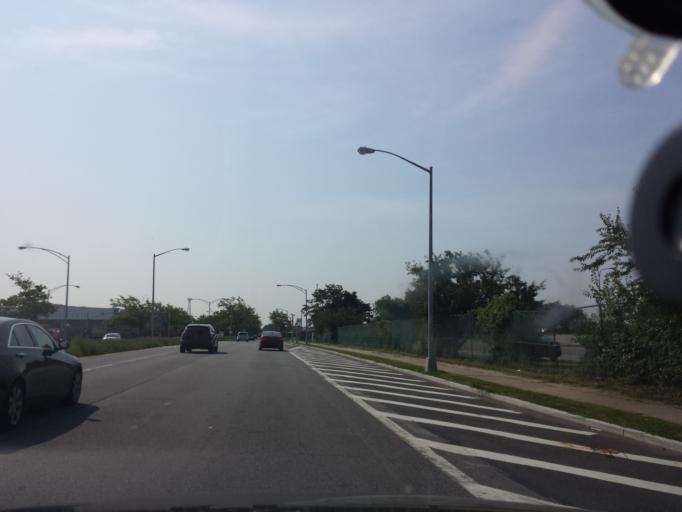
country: US
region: New York
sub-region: Kings County
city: Brooklyn
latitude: 40.5909
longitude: -73.9019
